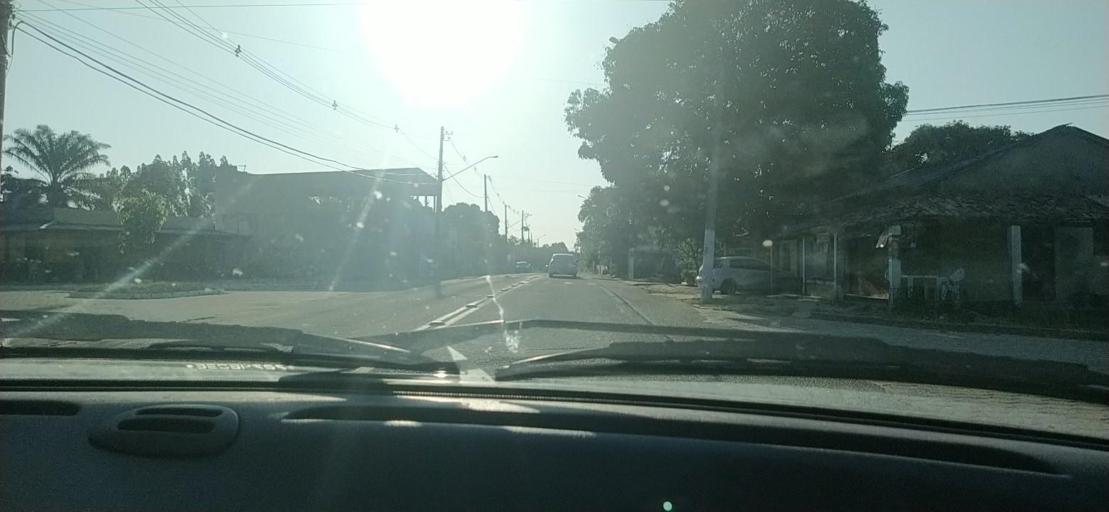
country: BR
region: Espirito Santo
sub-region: Conceicao Da Barra
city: Conceicao da Barra
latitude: -18.5668
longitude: -39.7587
